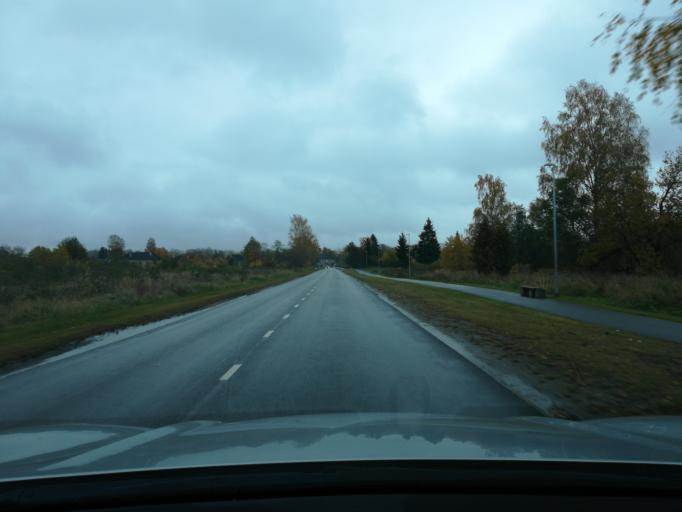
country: EE
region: Ida-Virumaa
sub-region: Johvi vald
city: Johvi
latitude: 59.3146
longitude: 27.4451
